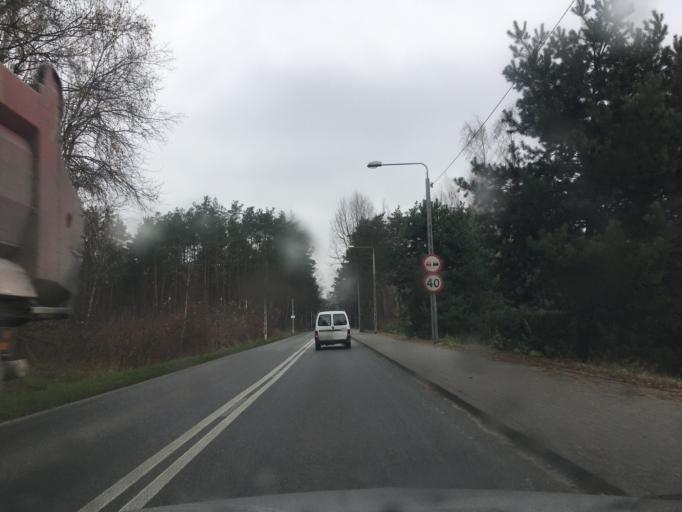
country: PL
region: Masovian Voivodeship
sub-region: Powiat piaseczynski
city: Lesznowola
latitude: 52.0596
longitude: 20.9199
